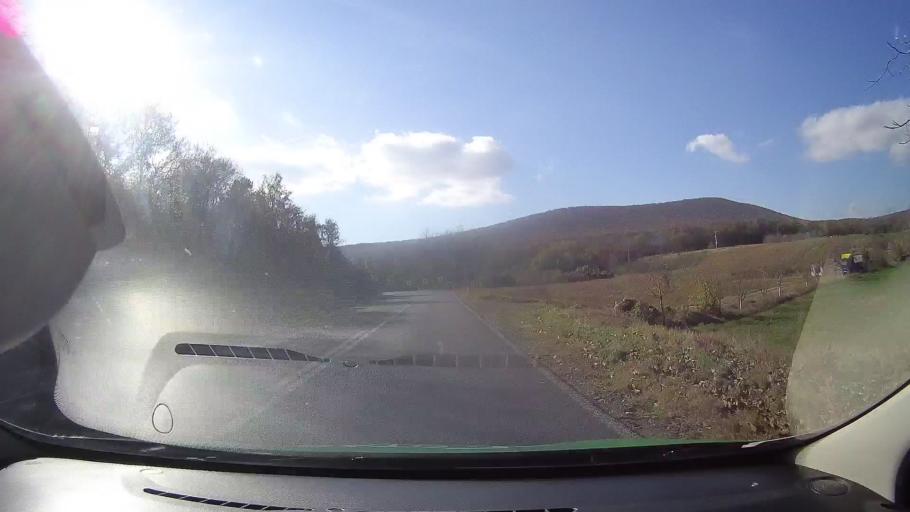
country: RO
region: Tulcea
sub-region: Oras Babadag
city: Babadag
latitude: 44.8749
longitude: 28.6896
